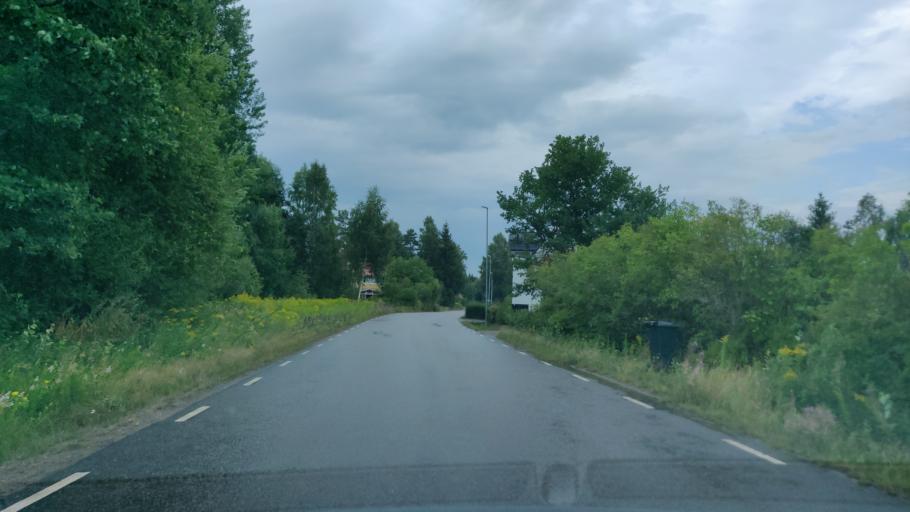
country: SE
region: Vaermland
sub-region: Munkfors Kommun
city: Munkfors
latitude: 59.8551
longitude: 13.5539
